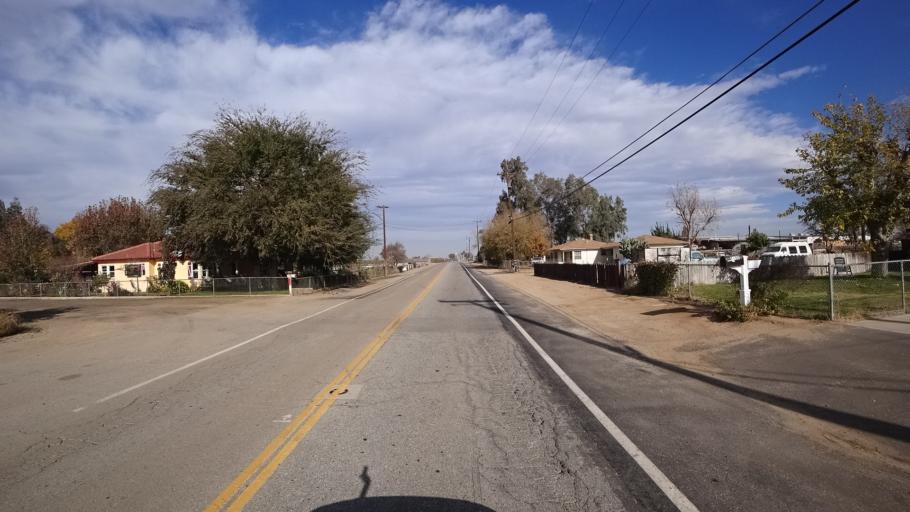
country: US
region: California
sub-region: Kern County
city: Greenacres
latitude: 35.4237
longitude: -119.0745
